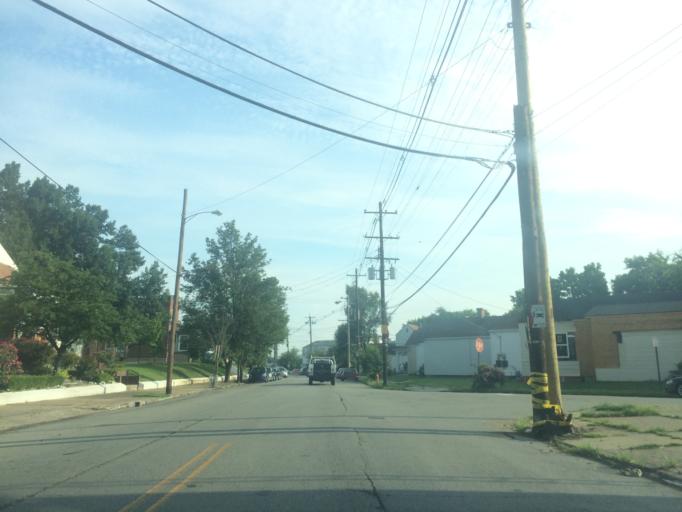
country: US
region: Kentucky
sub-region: Jefferson County
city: Audubon Park
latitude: 38.2266
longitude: -85.7417
